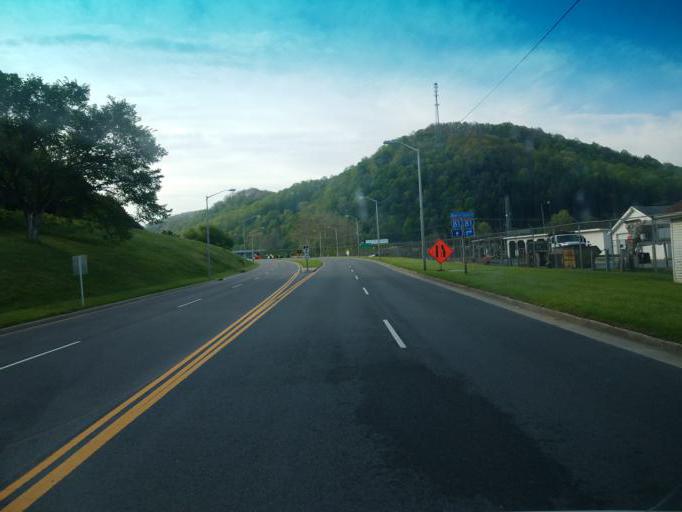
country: US
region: Virginia
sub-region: Smyth County
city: Marion
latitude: 36.8288
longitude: -81.5100
